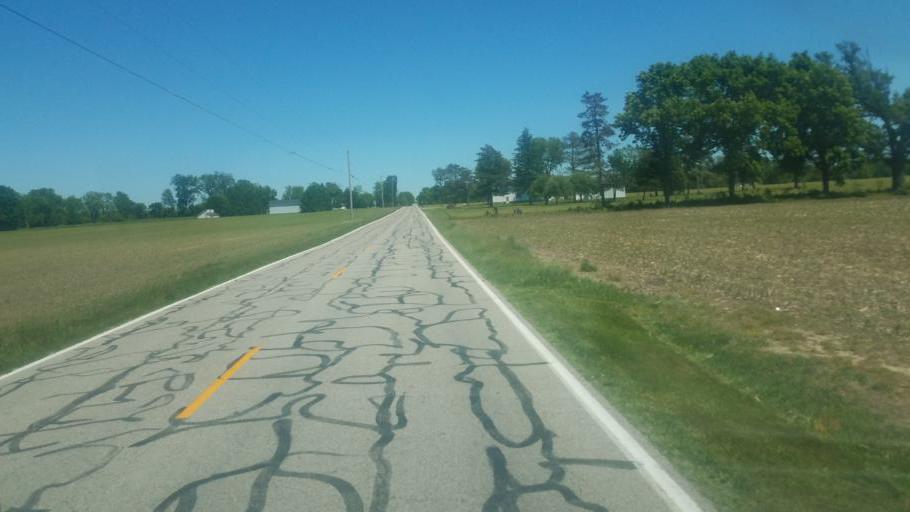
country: US
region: Ohio
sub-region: Shelby County
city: Sidney
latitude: 40.2150
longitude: -84.1775
